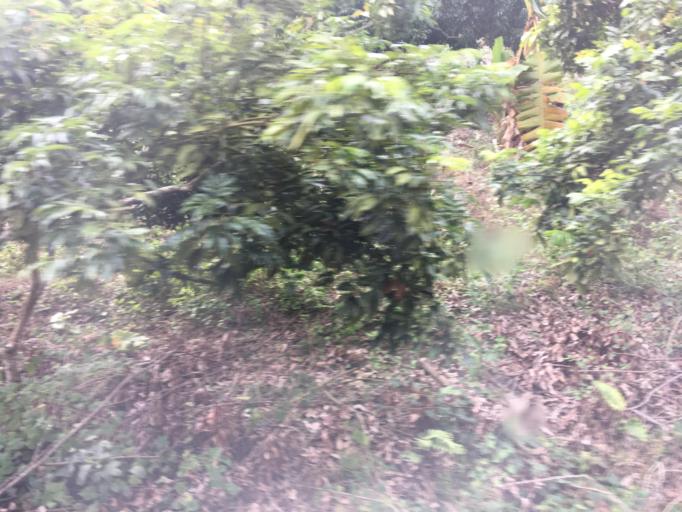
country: TW
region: Taiwan
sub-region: Chiayi
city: Jiayi Shi
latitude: 23.5403
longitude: 120.5649
